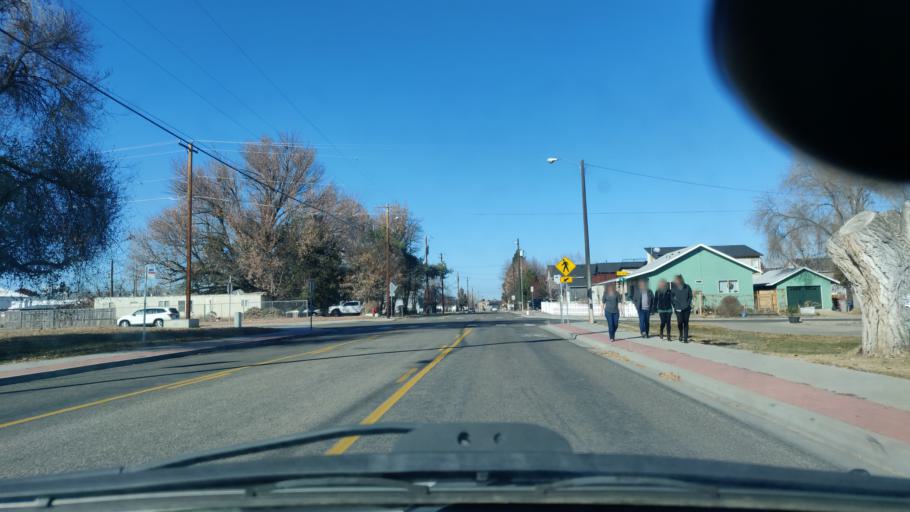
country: US
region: Idaho
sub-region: Ada County
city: Garden City
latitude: 43.6453
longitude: -116.2630
